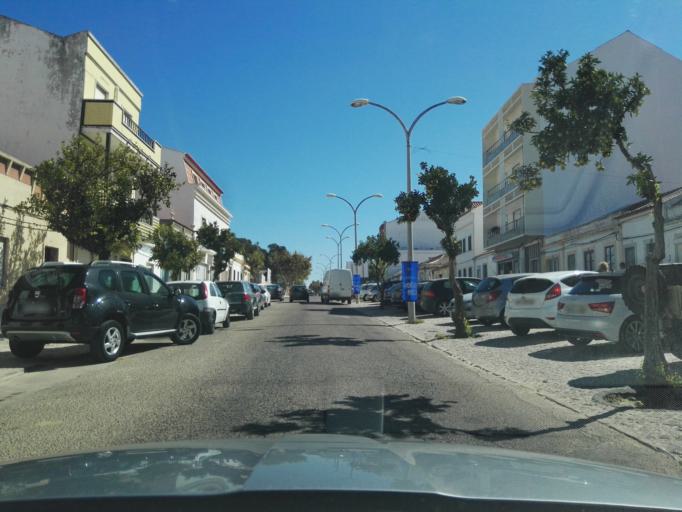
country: PT
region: Setubal
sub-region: Alcochete
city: Alcochete
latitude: 38.7560
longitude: -8.9587
